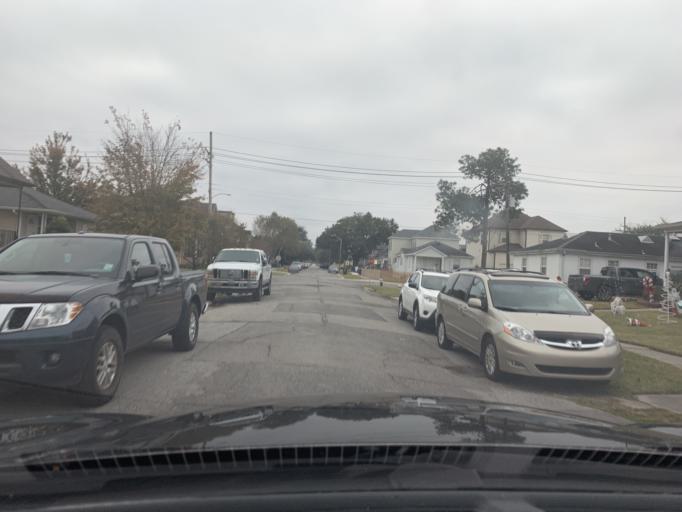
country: US
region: Louisiana
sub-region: Jefferson Parish
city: Metairie
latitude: 30.0076
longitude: -90.1111
